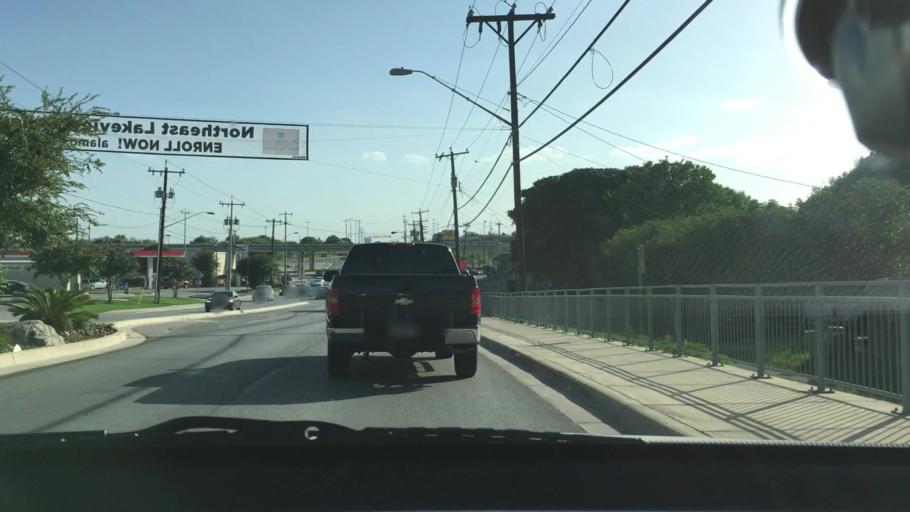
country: US
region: Texas
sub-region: Bexar County
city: Universal City
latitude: 29.5479
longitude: -98.3131
